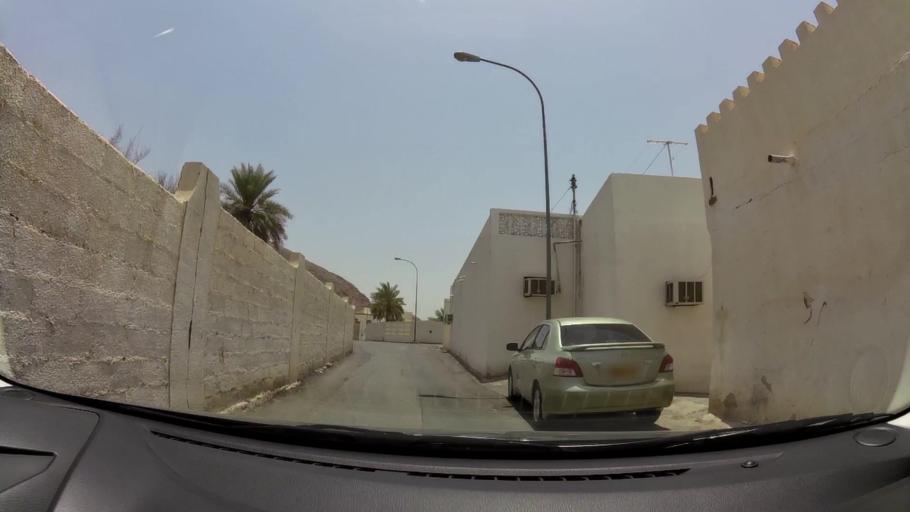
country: OM
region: Muhafazat Masqat
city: Bawshar
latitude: 23.5312
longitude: 58.3927
